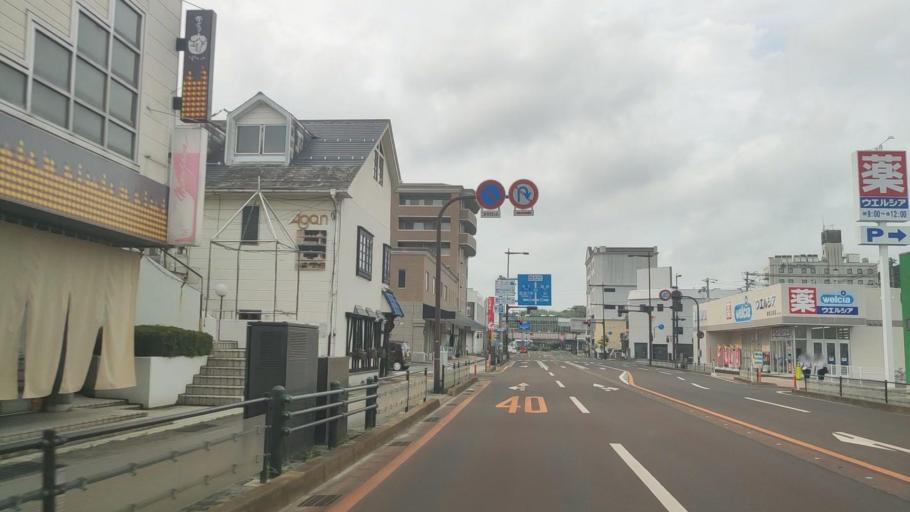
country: JP
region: Tottori
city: Kurayoshi
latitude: 35.4521
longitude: 133.8494
